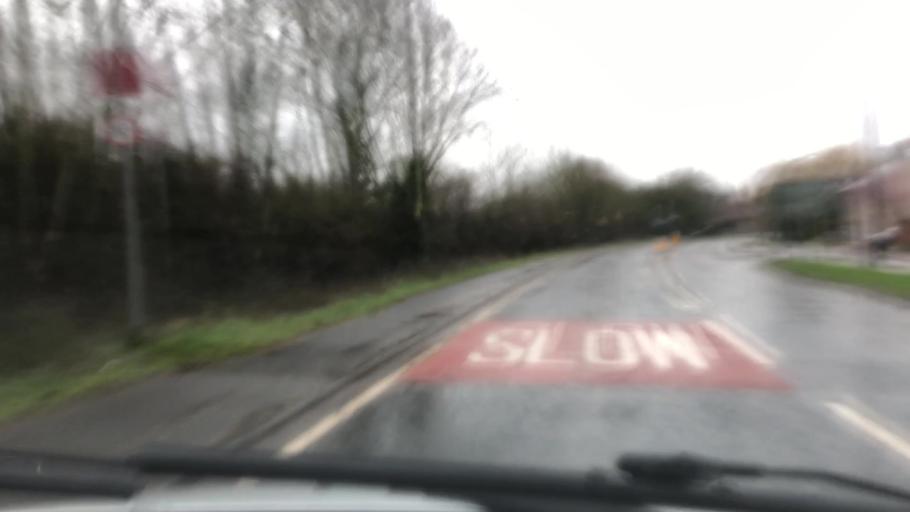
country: GB
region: England
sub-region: Hampshire
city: Odiham
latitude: 51.2650
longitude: -0.9527
